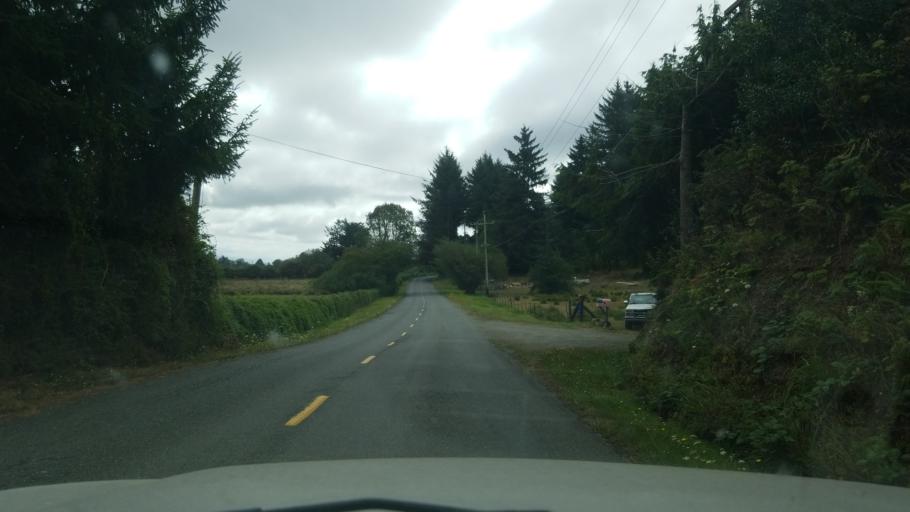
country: US
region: California
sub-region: Humboldt County
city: Ferndale
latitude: 40.5802
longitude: -124.2738
